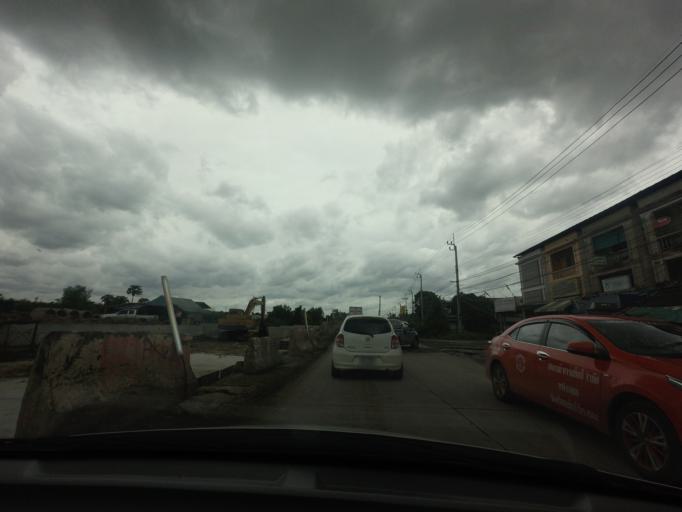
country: TH
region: Bangkok
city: Lat Krabang
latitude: 13.7634
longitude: 100.7761
